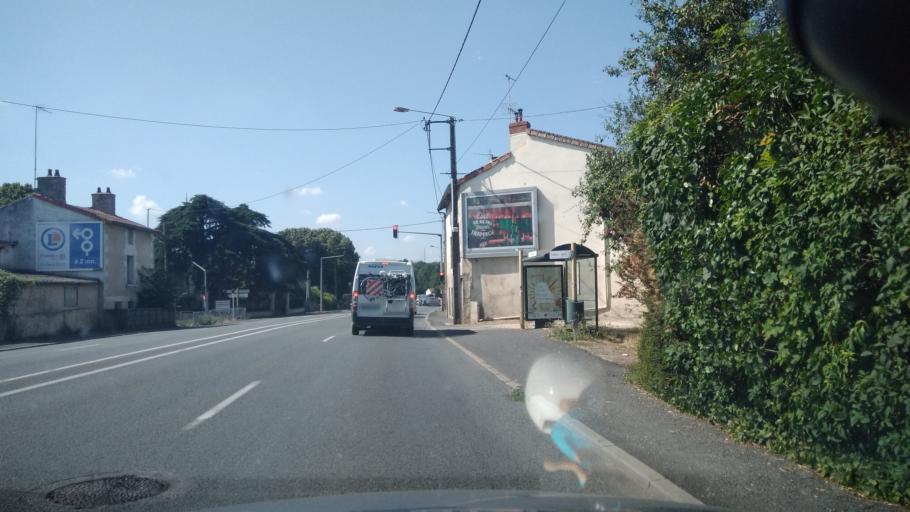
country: FR
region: Poitou-Charentes
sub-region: Departement de la Vienne
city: Chasseneuil-du-Poitou
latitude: 46.6397
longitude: 0.3590
